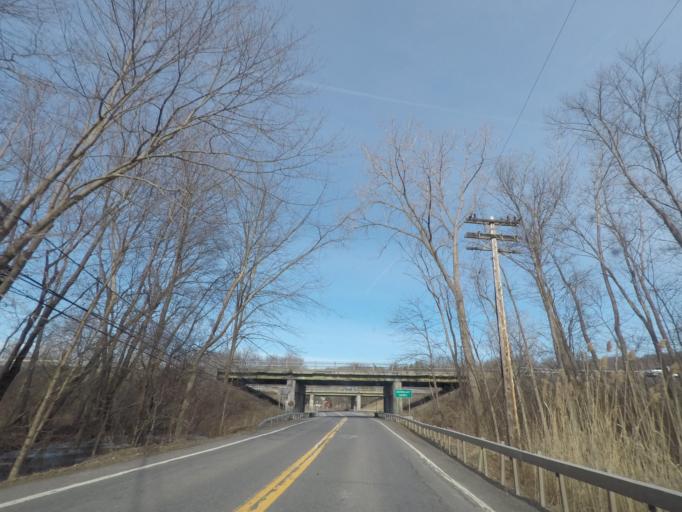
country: US
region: New York
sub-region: Rensselaer County
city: Nassau
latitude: 42.4798
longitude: -73.6258
